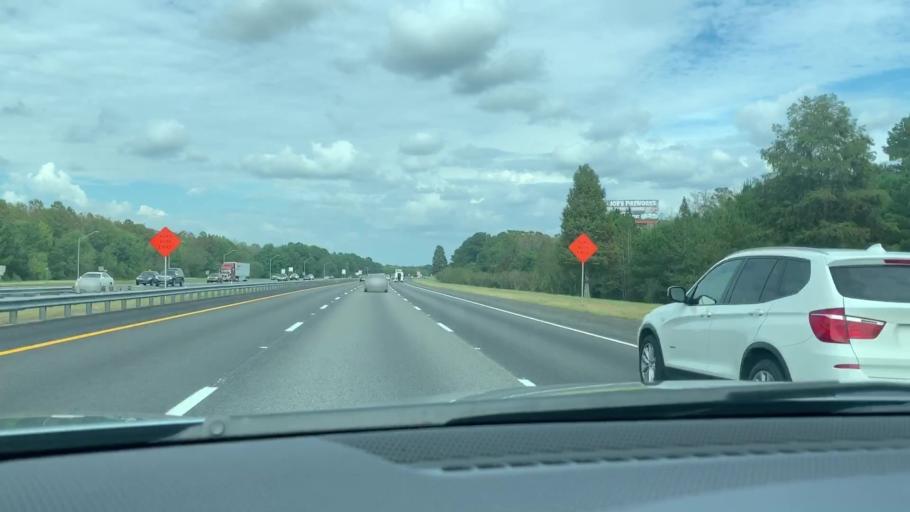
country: US
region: Georgia
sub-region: Chatham County
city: Port Wentworth
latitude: 32.2216
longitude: -81.1691
